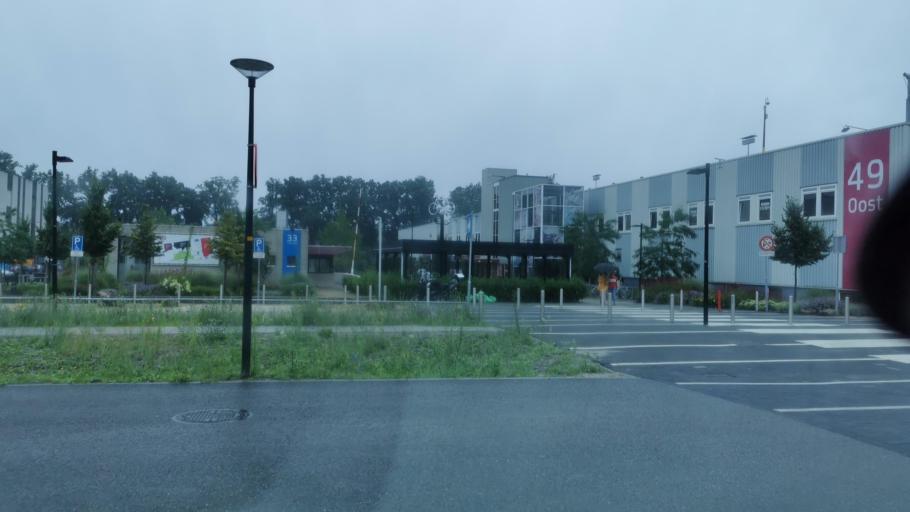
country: NL
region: Overijssel
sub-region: Gemeente Enschede
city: Enschede
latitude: 52.2221
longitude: 6.9032
